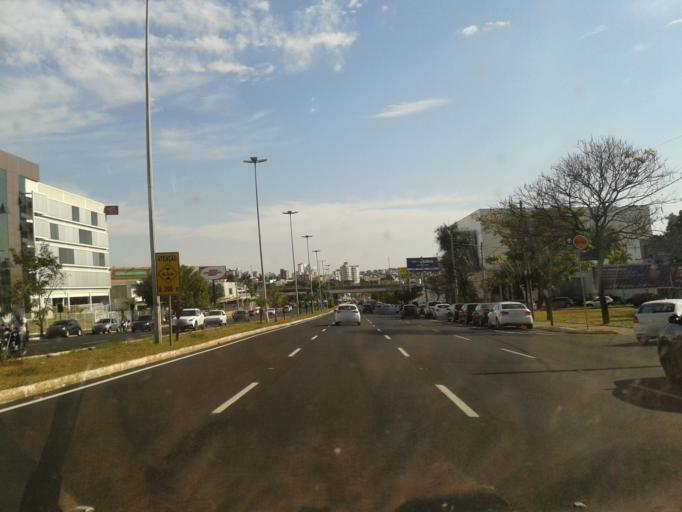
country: BR
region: Minas Gerais
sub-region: Uberlandia
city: Uberlandia
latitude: -18.9286
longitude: -48.2759
